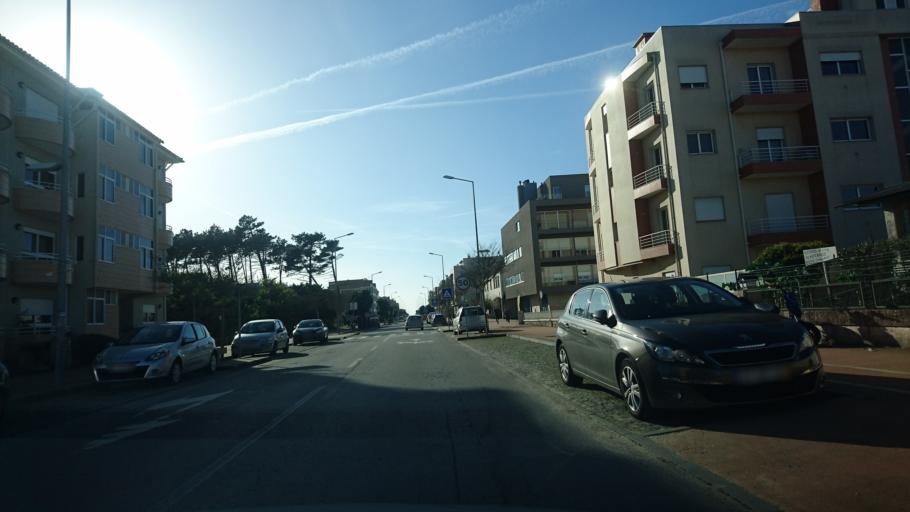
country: PT
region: Aveiro
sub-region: Ovar
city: Esmoriz
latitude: 40.9544
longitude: -8.6450
